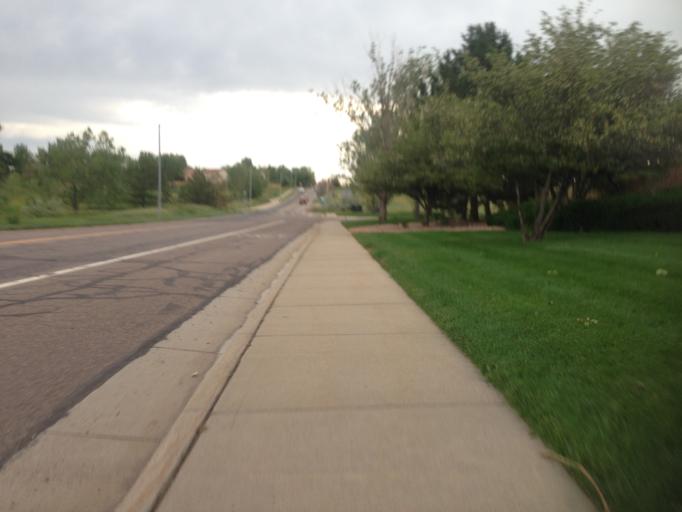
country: US
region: Colorado
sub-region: Boulder County
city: Superior
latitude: 39.9386
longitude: -105.1470
